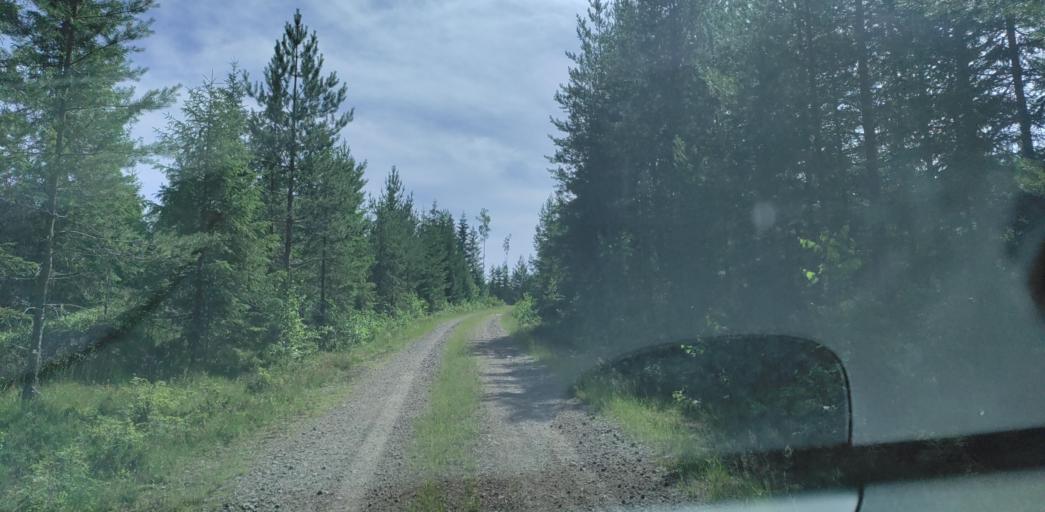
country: SE
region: Vaermland
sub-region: Hagfors Kommun
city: Ekshaerad
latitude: 60.0983
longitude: 13.3720
